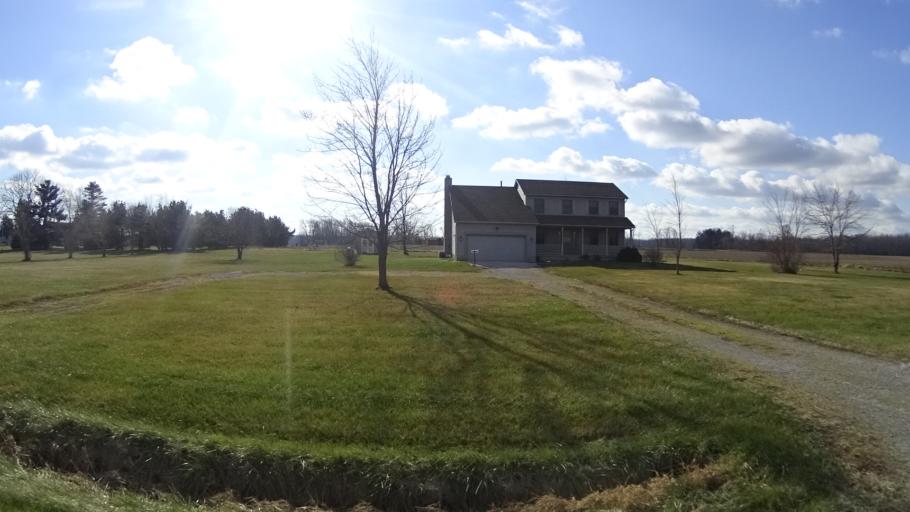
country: US
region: Ohio
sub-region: Lorain County
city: Camden
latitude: 41.2047
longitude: -82.2678
